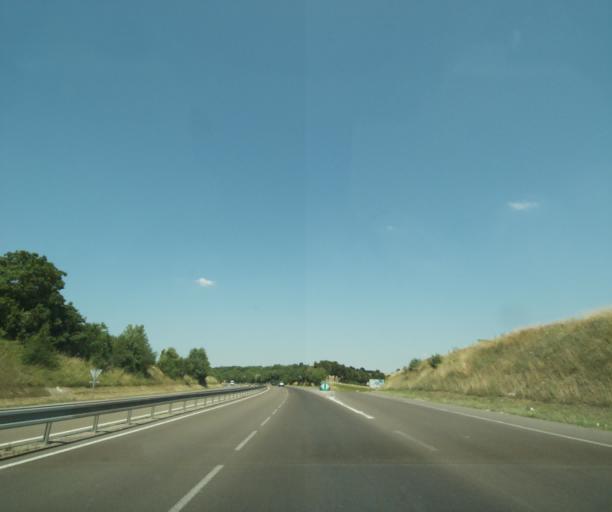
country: FR
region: Champagne-Ardenne
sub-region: Departement de la Marne
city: Saint-Memmie
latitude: 48.9744
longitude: 4.3785
